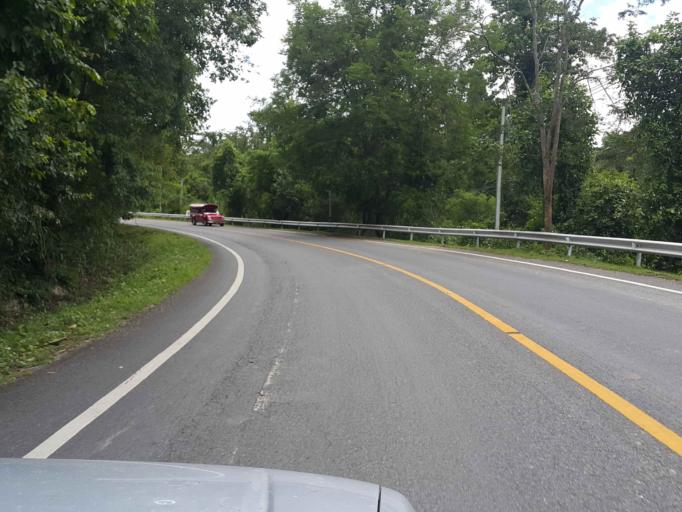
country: TH
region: Chiang Mai
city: Chom Thong
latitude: 18.5247
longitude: 98.6519
